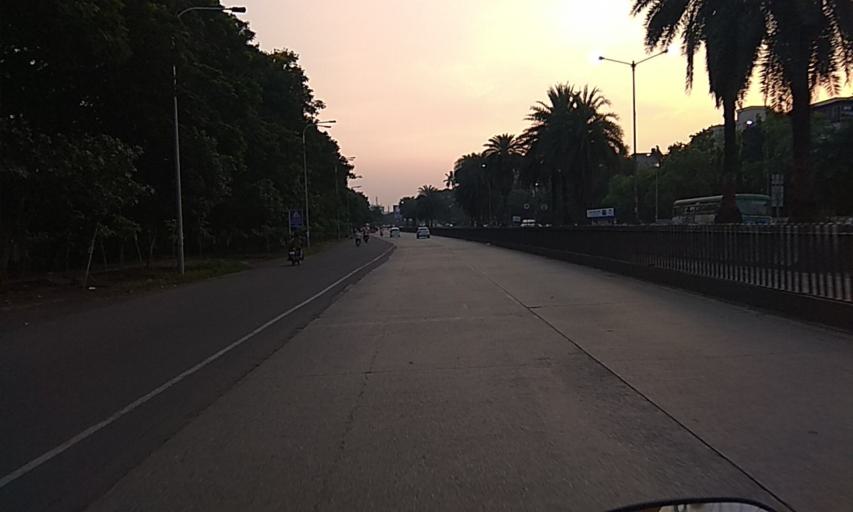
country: IN
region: Maharashtra
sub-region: Pune Division
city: Khadki
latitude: 18.5503
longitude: 73.8941
